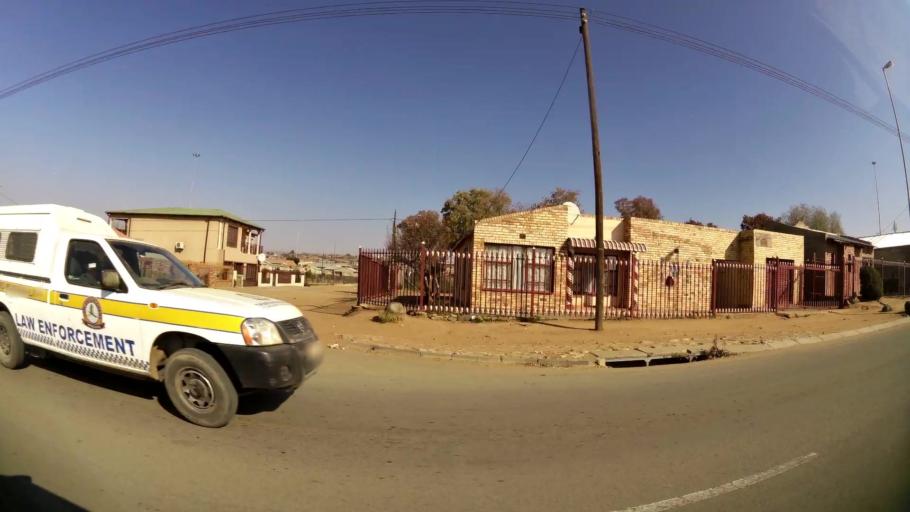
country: ZA
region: Orange Free State
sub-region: Mangaung Metropolitan Municipality
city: Bloemfontein
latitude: -29.1841
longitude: 26.2444
